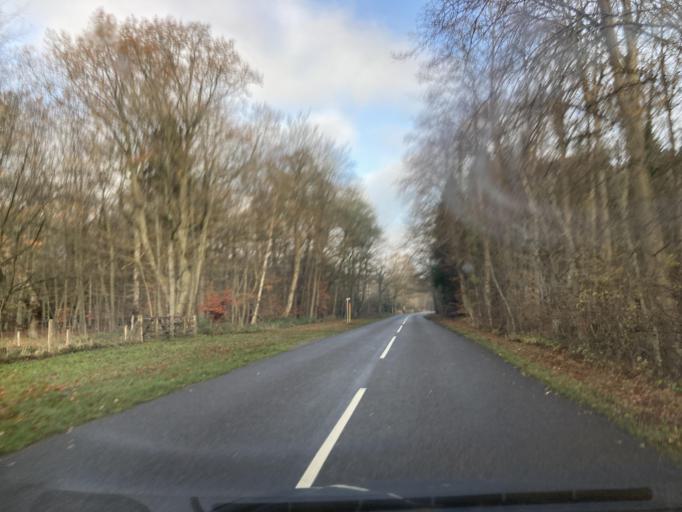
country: DK
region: Zealand
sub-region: Lolland Kommune
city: Rodby
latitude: 54.7759
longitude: 11.3674
